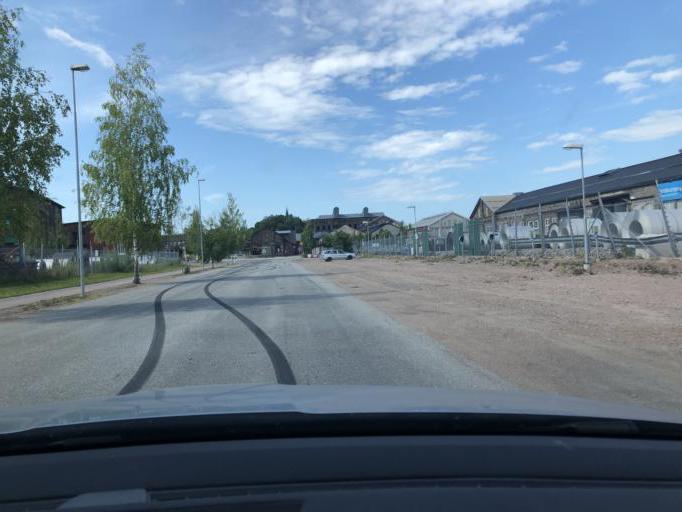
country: SE
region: Dalarna
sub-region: Avesta Kommun
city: Avesta
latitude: 60.1477
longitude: 16.1774
